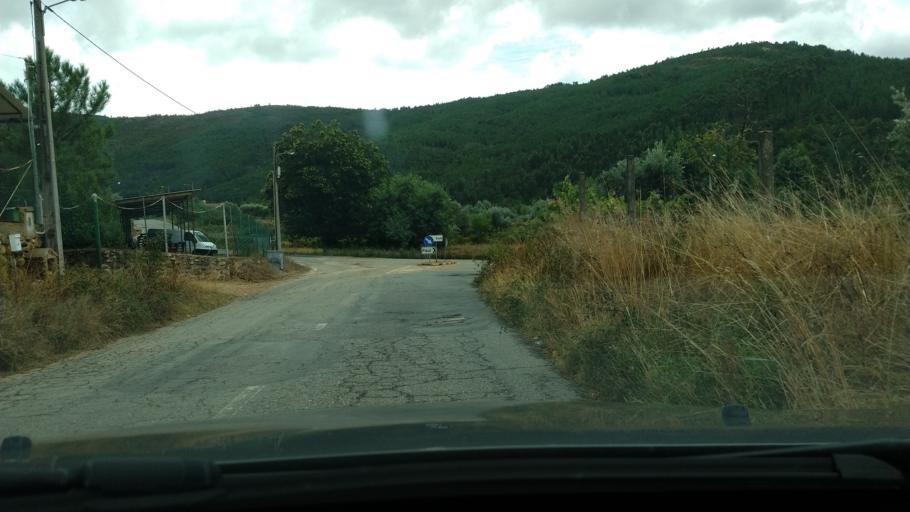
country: PT
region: Castelo Branco
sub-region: Concelho do Fundao
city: Aldeia de Joanes
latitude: 40.2169
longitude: -7.6275
